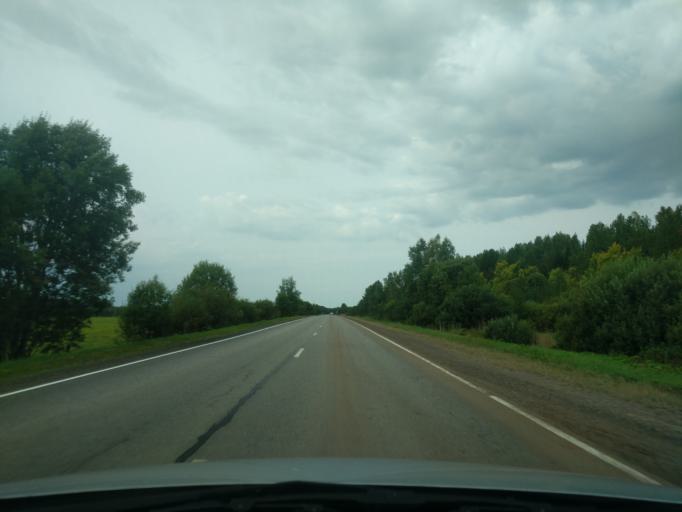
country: RU
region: Kirov
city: Svecha
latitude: 58.2737
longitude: 47.7498
